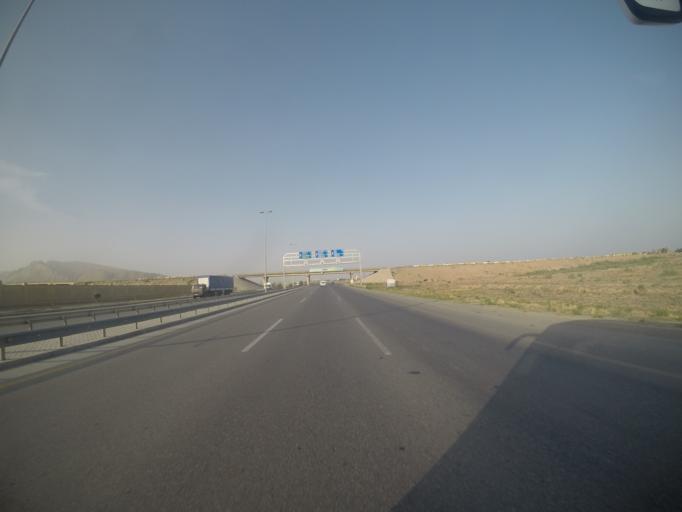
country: AZ
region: Baki
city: Korgoz
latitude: 40.2498
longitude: 49.6163
